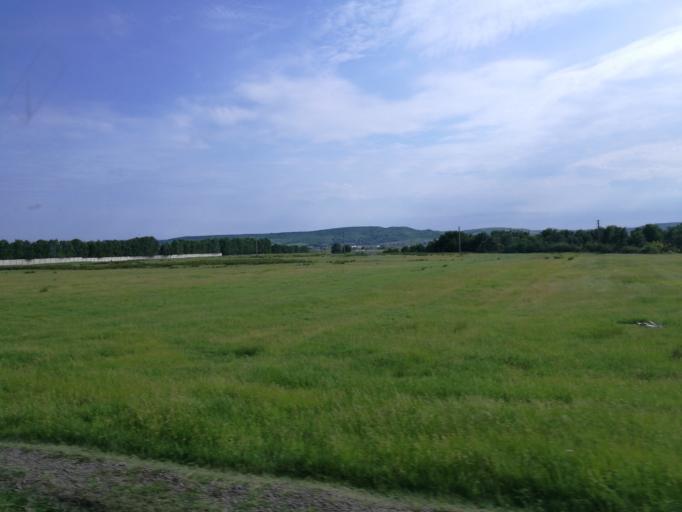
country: RO
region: Arges
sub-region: Comuna Bradu
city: Geamana
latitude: 44.8350
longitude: 24.9096
